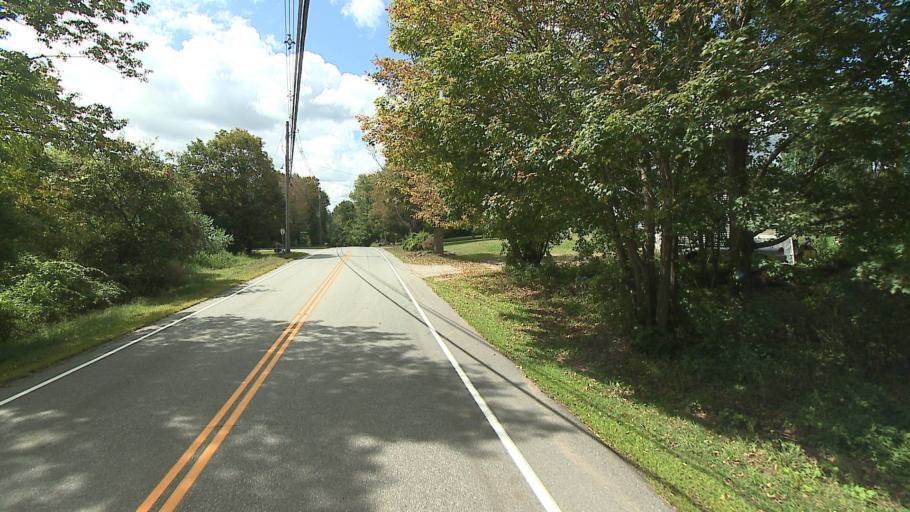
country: US
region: Connecticut
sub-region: Tolland County
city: Storrs
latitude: 41.8406
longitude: -72.2253
